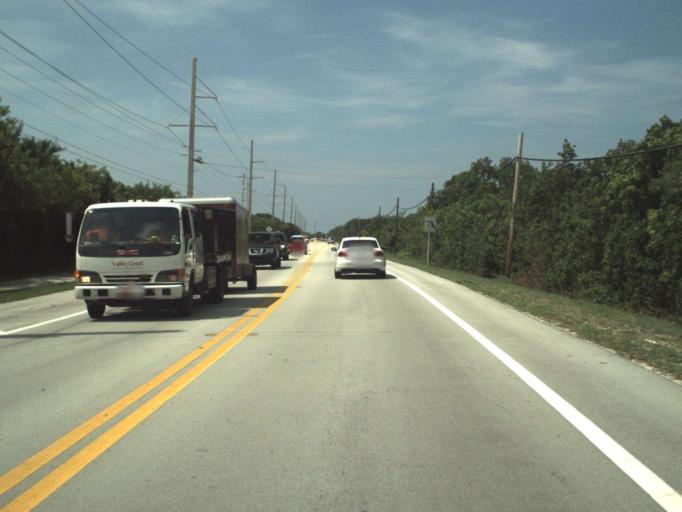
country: US
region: Florida
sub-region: Monroe County
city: Islamorada
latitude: 24.8195
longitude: -80.8219
